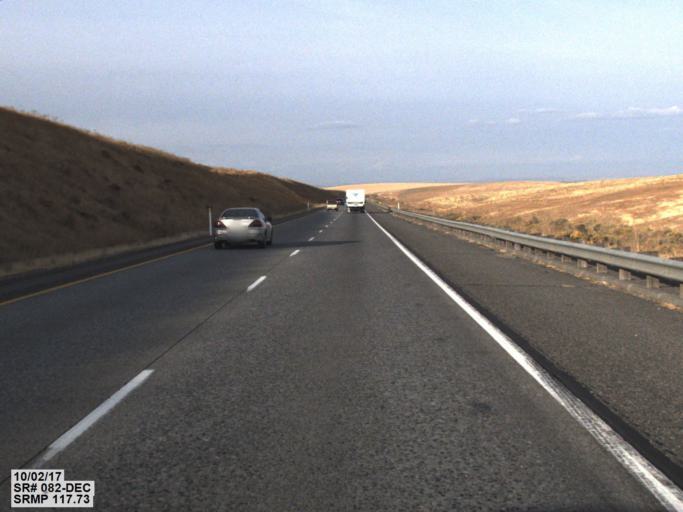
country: US
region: Washington
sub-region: Benton County
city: Highland
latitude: 46.0974
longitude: -119.2193
